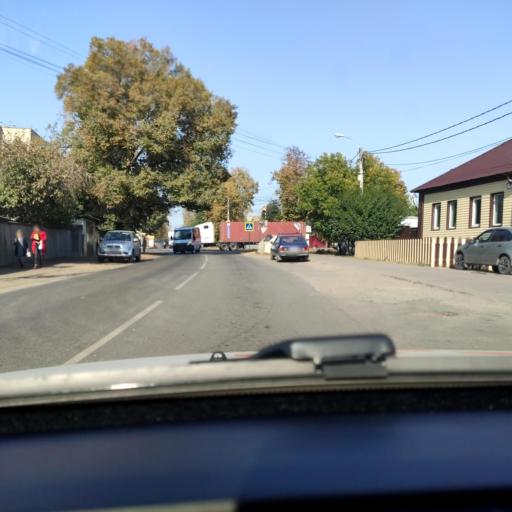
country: RU
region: Voronezj
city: Voronezh
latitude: 51.6334
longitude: 39.1896
